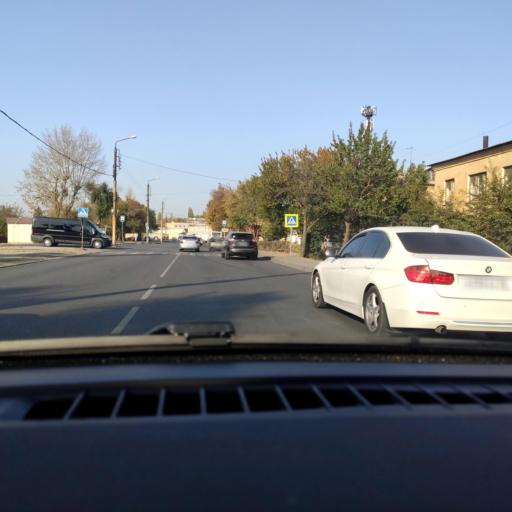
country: RU
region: Voronezj
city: Voronezh
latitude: 51.6240
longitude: 39.1764
